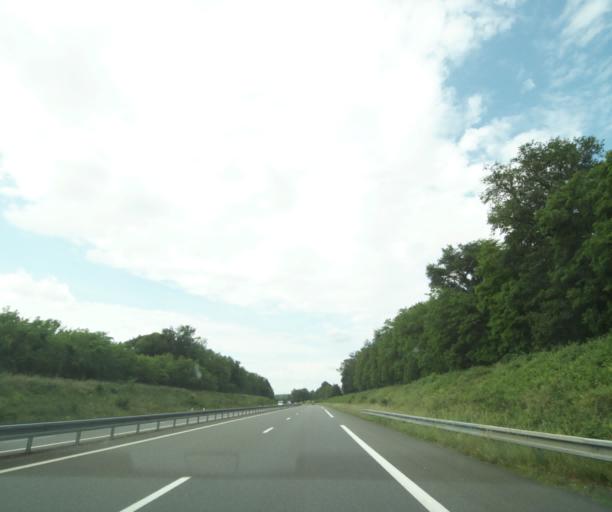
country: FR
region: Pays de la Loire
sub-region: Departement de Maine-et-Loire
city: Brion
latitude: 47.4472
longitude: -0.1768
